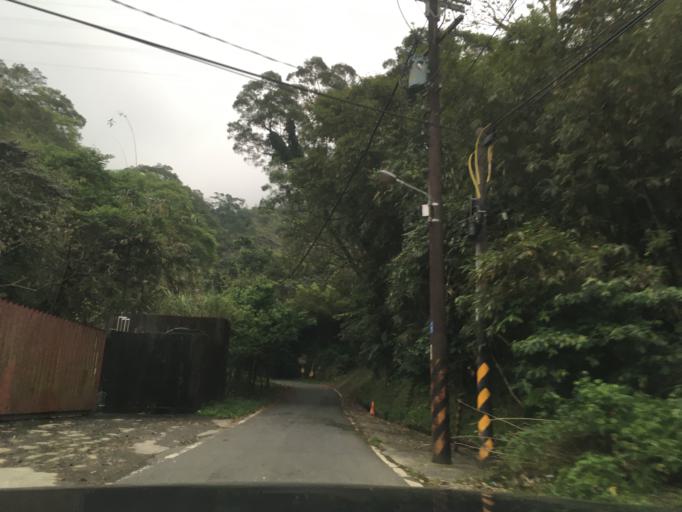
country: TW
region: Taiwan
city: Daxi
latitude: 24.8940
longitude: 121.3796
